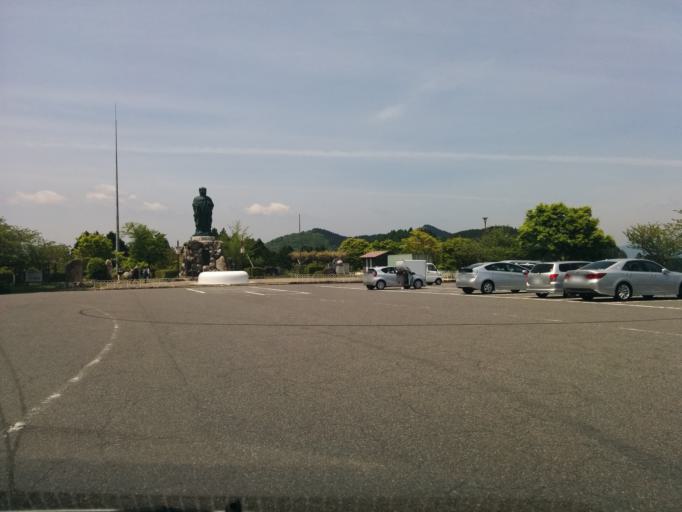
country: JP
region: Shiga Prefecture
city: Otsu-shi
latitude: 35.0795
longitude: 135.8394
